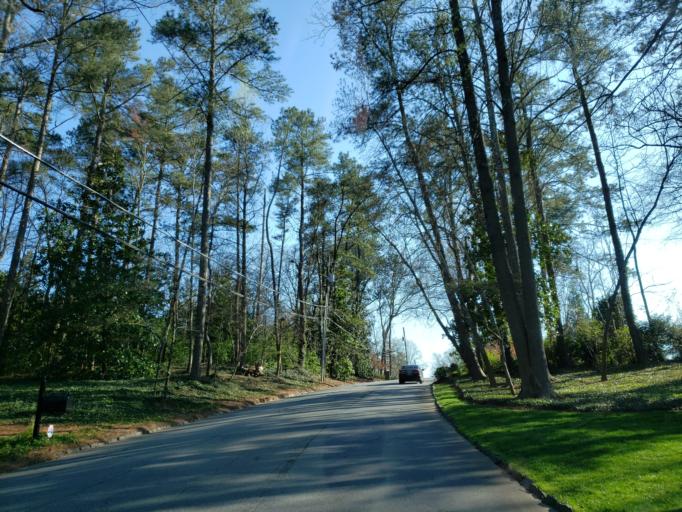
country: US
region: Georgia
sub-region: DeKalb County
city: North Atlanta
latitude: 33.8527
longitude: -84.3987
